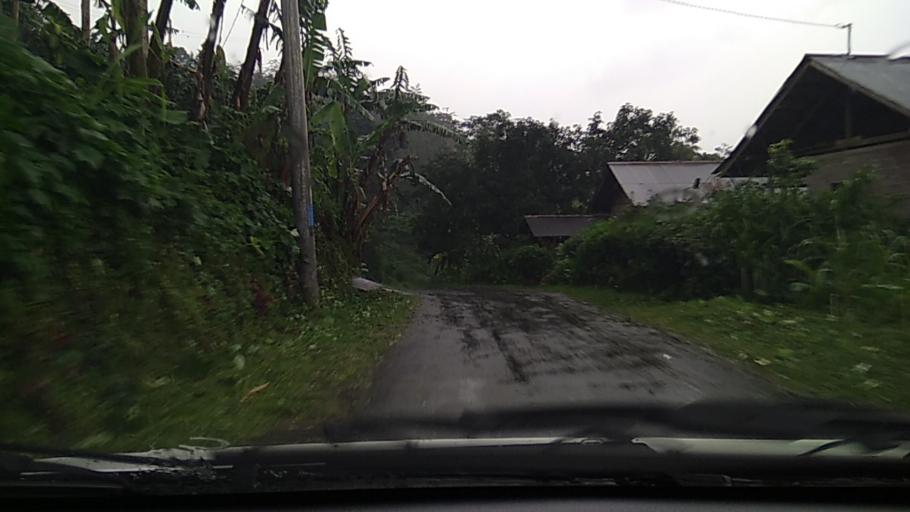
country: ID
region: Bali
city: Banjar Ambengan
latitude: -8.2194
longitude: 115.1659
